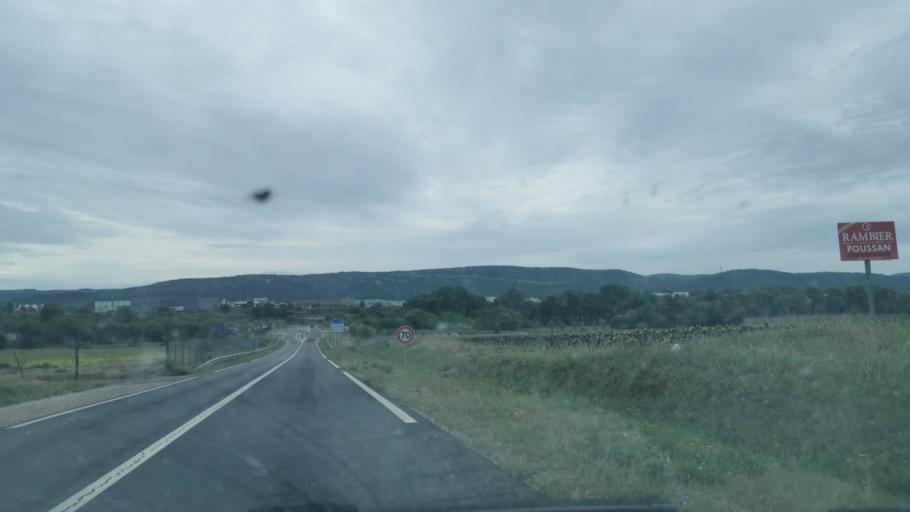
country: FR
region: Languedoc-Roussillon
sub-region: Departement de l'Herault
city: Gigean
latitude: 43.4965
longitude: 3.6938
